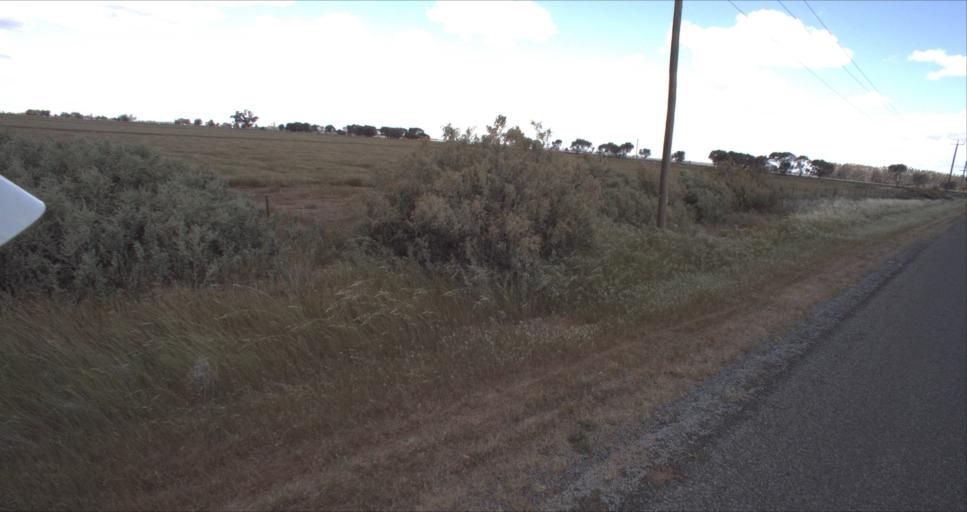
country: AU
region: New South Wales
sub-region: Leeton
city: Leeton
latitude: -34.5284
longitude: 146.2197
